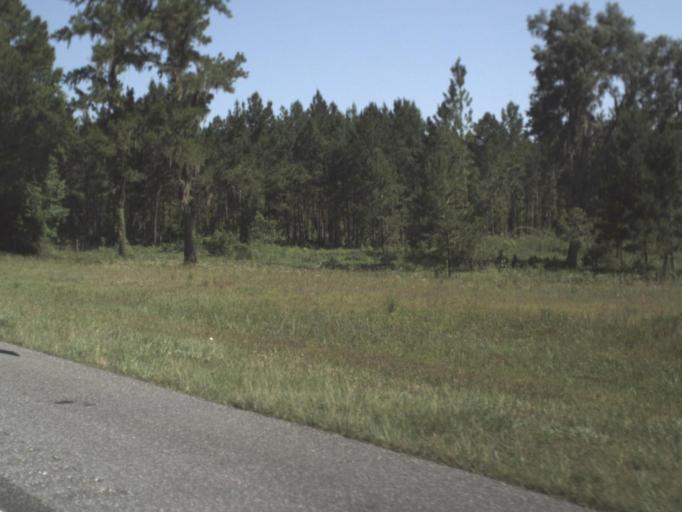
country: US
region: Florida
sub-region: Suwannee County
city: Live Oak
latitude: 30.3232
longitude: -82.9521
